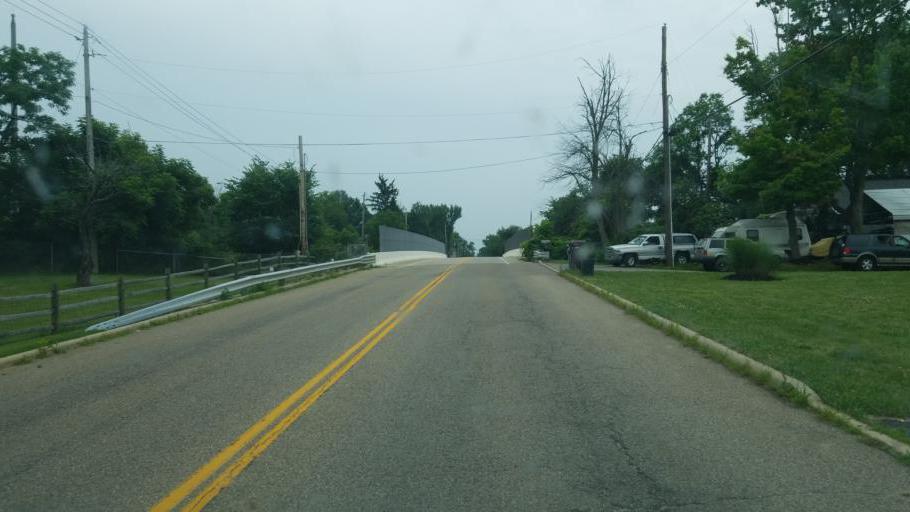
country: US
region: Ohio
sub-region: Summit County
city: Mogadore
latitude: 41.0719
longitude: -81.4172
